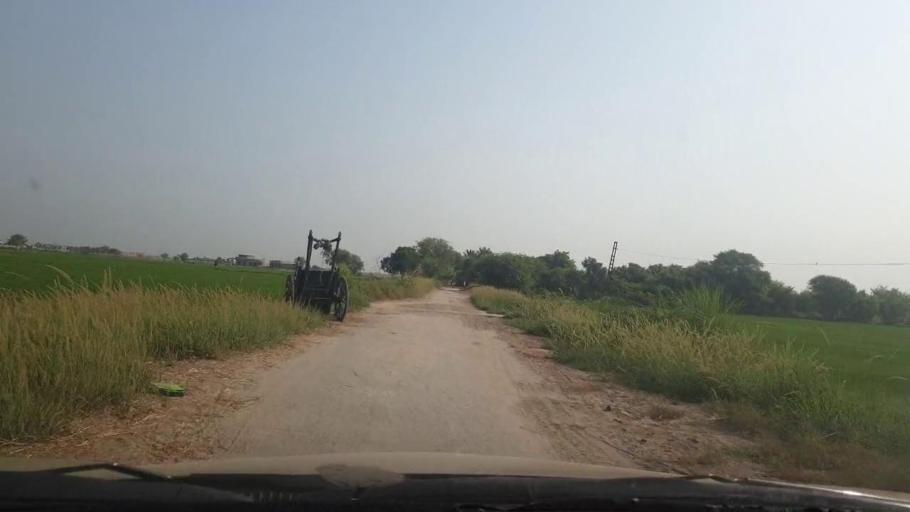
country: PK
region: Sindh
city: Larkana
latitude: 27.5860
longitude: 68.1870
